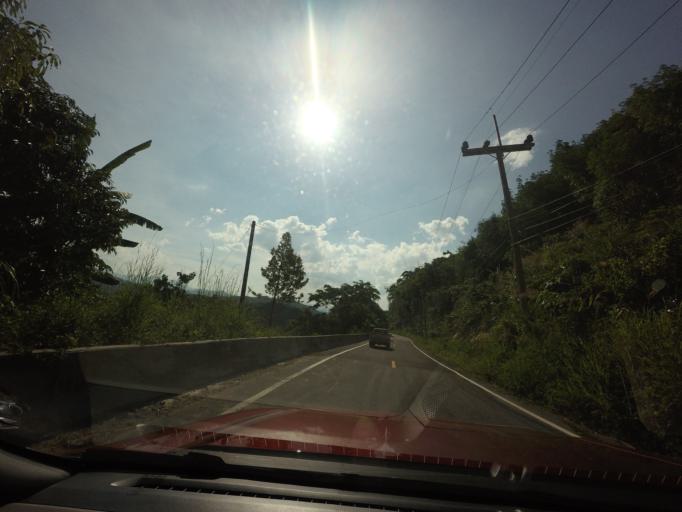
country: TH
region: Yala
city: Than To
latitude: 6.0782
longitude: 101.3345
